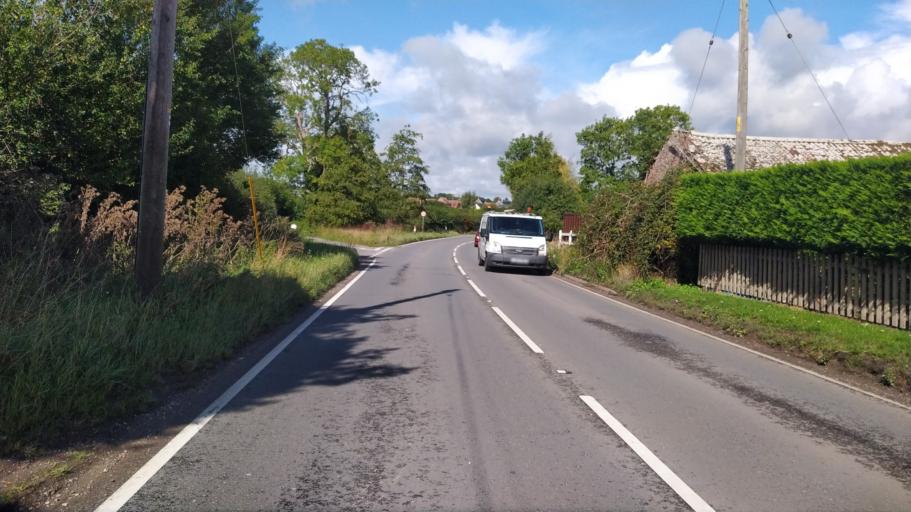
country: GB
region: England
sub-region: Dorset
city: Manston
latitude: 50.8924
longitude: -2.2374
